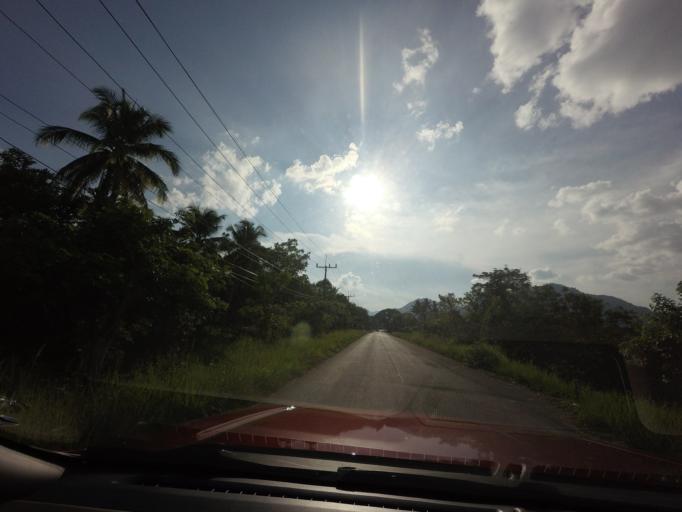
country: TH
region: Yala
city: Ban Nang Sata
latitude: 6.2230
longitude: 101.2264
